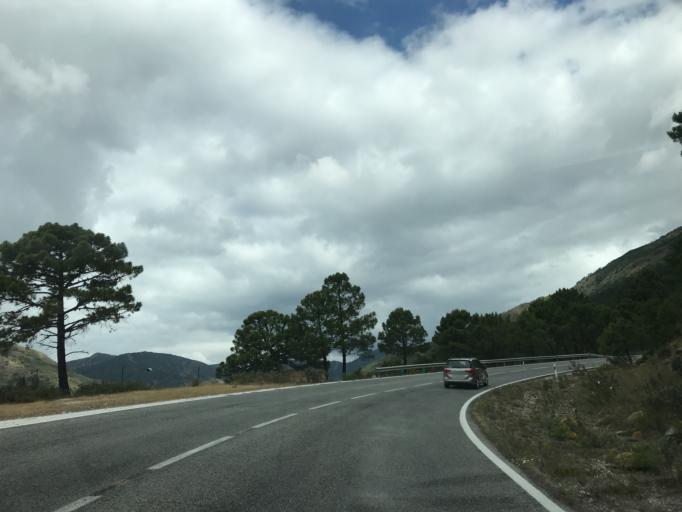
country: ES
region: Andalusia
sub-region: Provincia de Malaga
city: Benahavis
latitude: 36.5594
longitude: -5.0586
